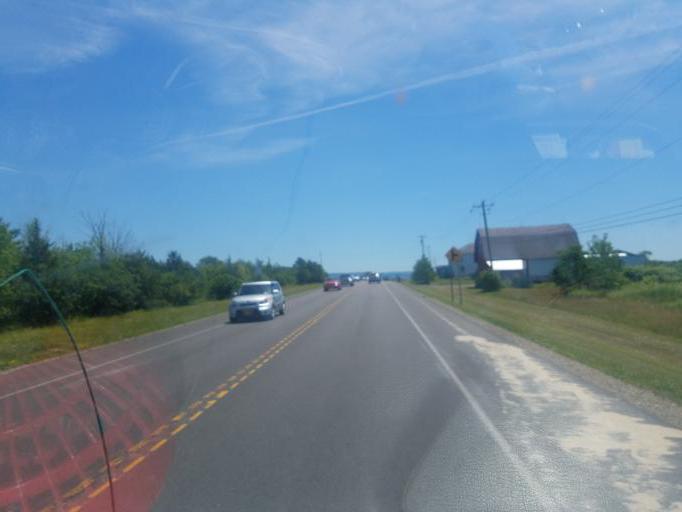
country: US
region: New York
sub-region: Yates County
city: Dundee
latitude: 42.5895
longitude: -76.9393
